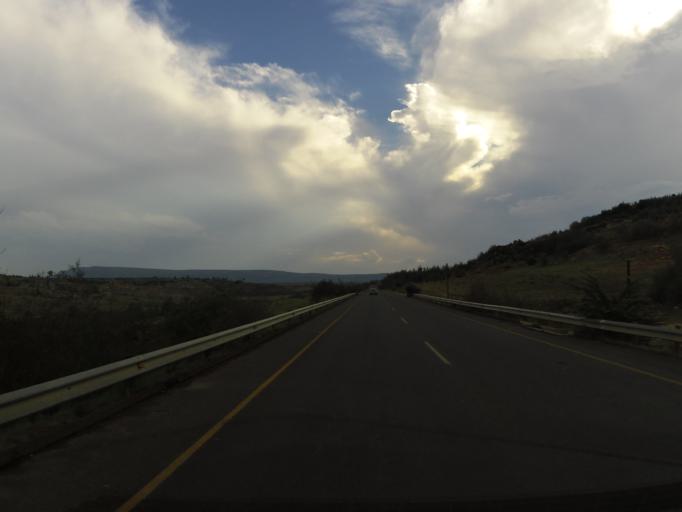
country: LS
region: Maseru
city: Maseru
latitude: -29.3967
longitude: 27.5367
